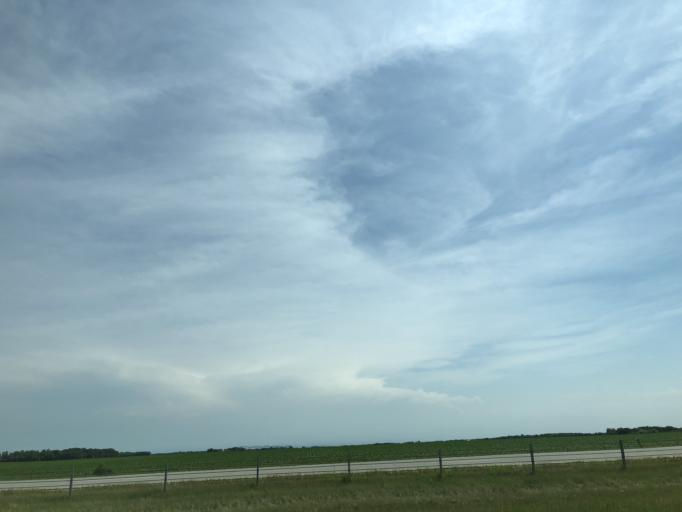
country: US
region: Minnesota
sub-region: Douglas County
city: Alexandria
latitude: 45.8327
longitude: -95.2916
